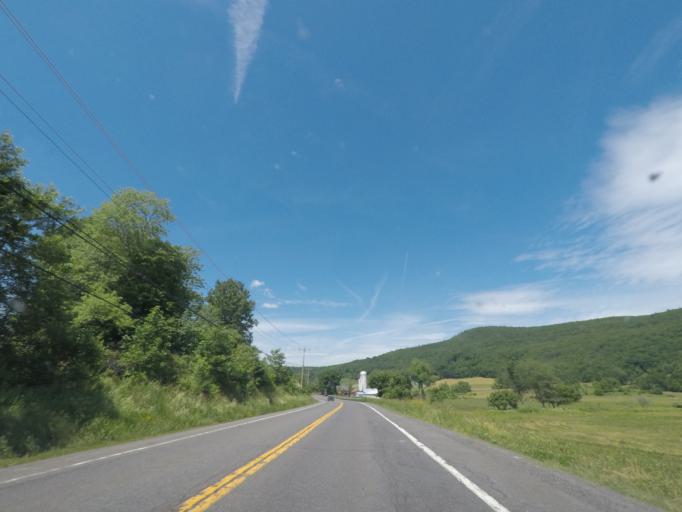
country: US
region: Massachusetts
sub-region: Berkshire County
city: Housatonic
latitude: 42.2474
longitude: -73.5064
